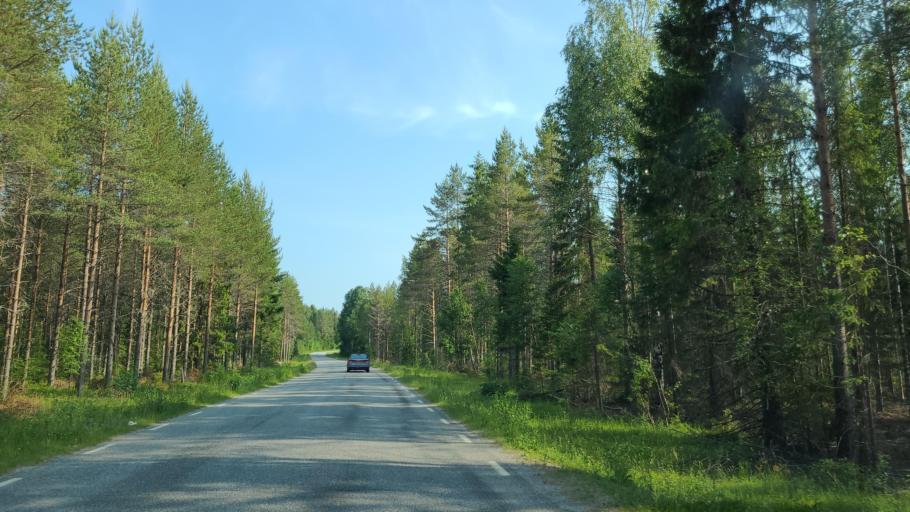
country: SE
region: Vaesterbotten
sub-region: Skelleftea Kommun
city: Burea
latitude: 64.3605
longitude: 21.3348
